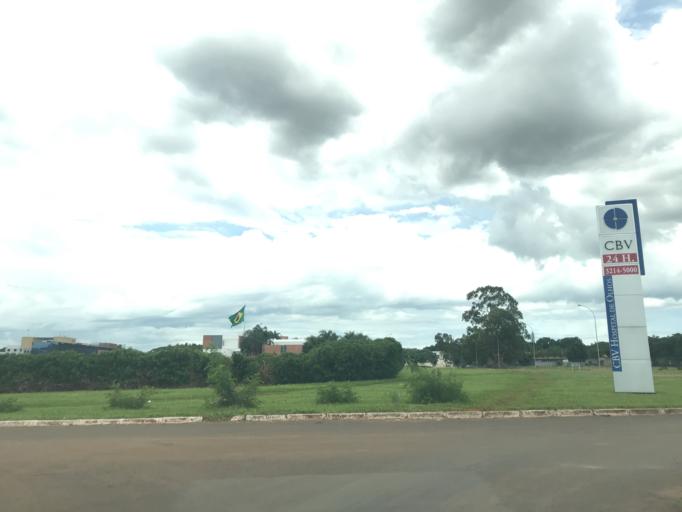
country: BR
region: Federal District
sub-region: Brasilia
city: Brasilia
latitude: -15.8352
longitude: -47.9087
